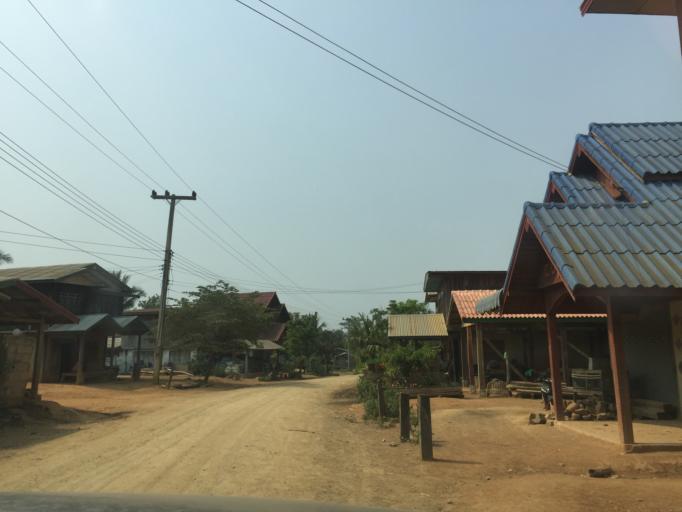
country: TH
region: Uttaradit
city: Ban Khok
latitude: 17.9490
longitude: 101.2834
